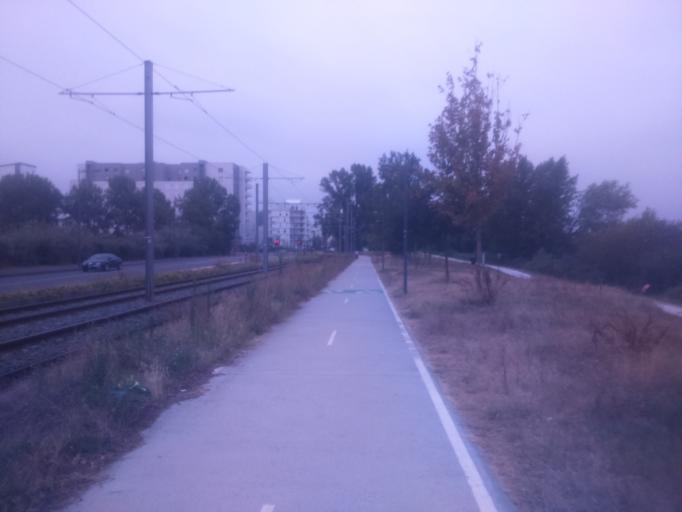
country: FR
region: Aquitaine
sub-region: Departement de la Gironde
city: Le Bouscat
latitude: 44.8847
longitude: -0.5717
